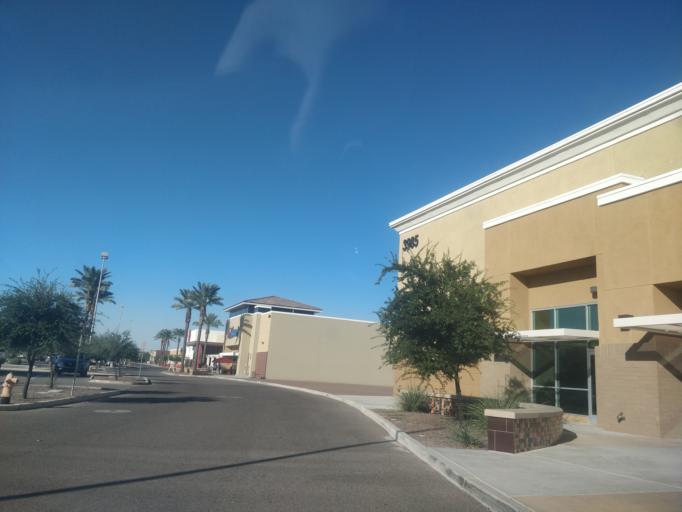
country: US
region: Arizona
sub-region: Maricopa County
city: Sun Lakes
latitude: 33.2486
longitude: -111.8385
